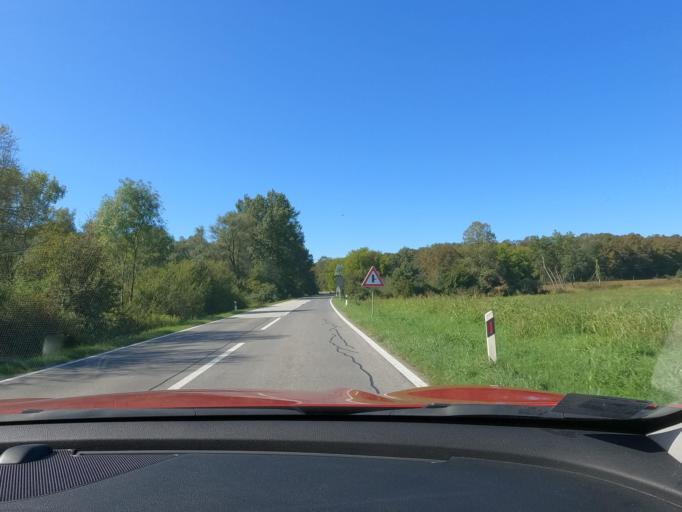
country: HR
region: Sisacko-Moslavacka
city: Osekovo
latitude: 45.5237
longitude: 16.5353
